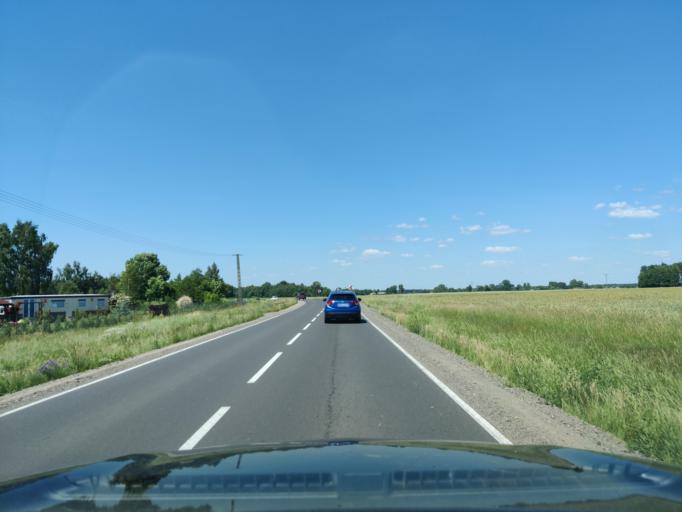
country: PL
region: Masovian Voivodeship
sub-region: Powiat plonski
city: Baboszewo
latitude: 52.7092
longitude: 20.3378
